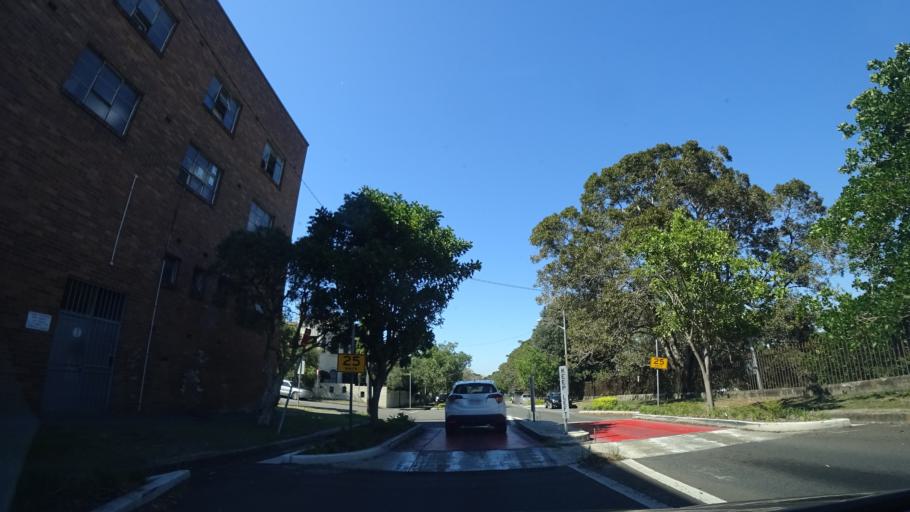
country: AU
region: New South Wales
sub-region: Waverley
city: Bondi Junction
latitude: -33.8927
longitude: 151.2414
